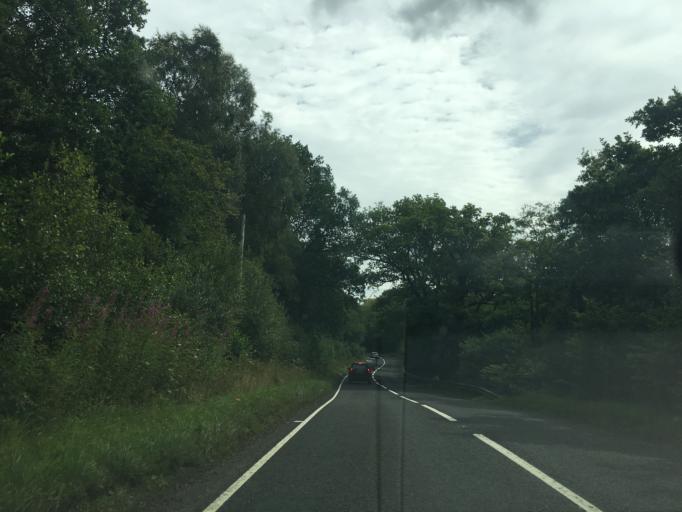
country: GB
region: Scotland
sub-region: Stirling
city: Callander
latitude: 56.2511
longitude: -4.2616
